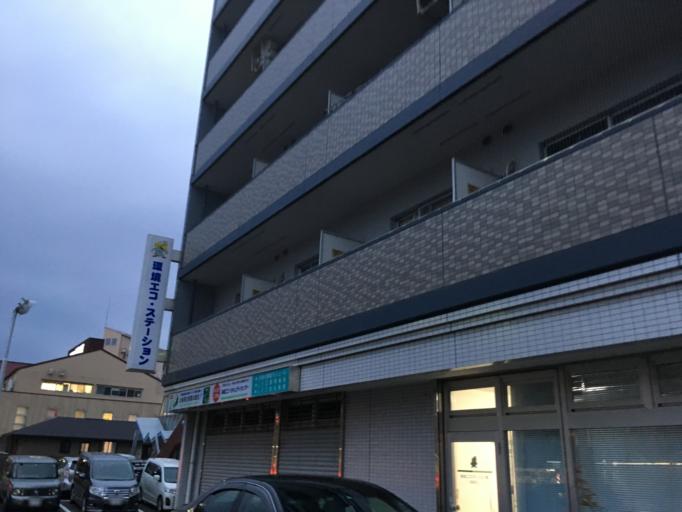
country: JP
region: Kumamoto
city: Kumamoto
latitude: 32.7958
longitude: 130.7262
